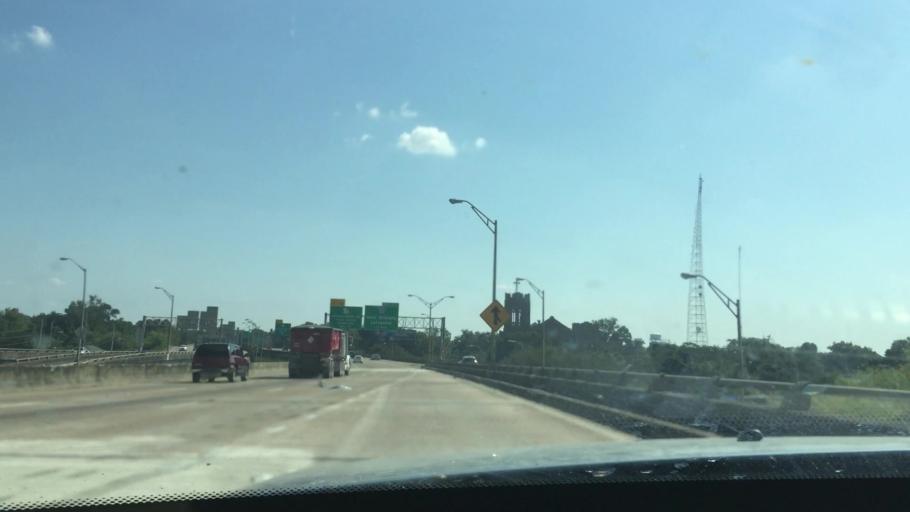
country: US
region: Louisiana
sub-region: East Baton Rouge Parish
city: Baton Rouge
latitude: 30.4492
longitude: -91.1806
